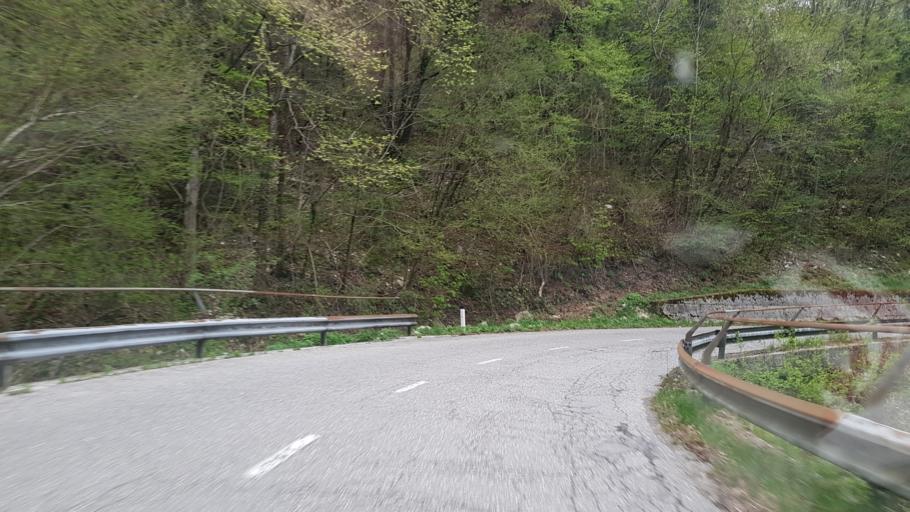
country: IT
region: Friuli Venezia Giulia
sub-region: Provincia di Udine
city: Pulfero
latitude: 46.2559
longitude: 13.4553
